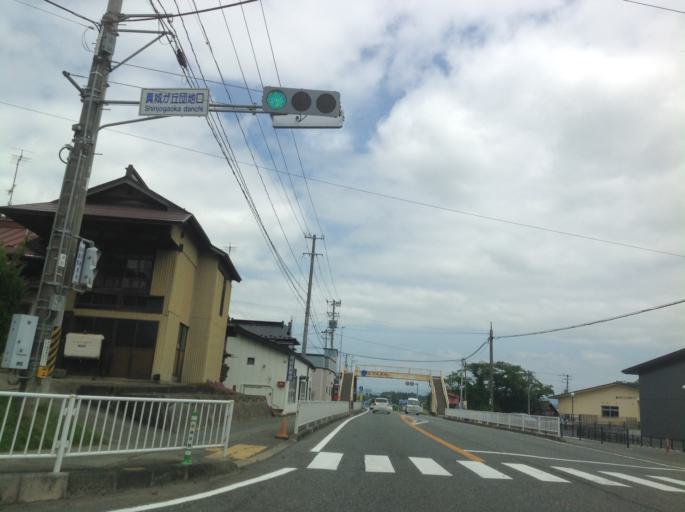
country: JP
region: Iwate
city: Mizusawa
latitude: 39.1137
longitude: 141.1441
